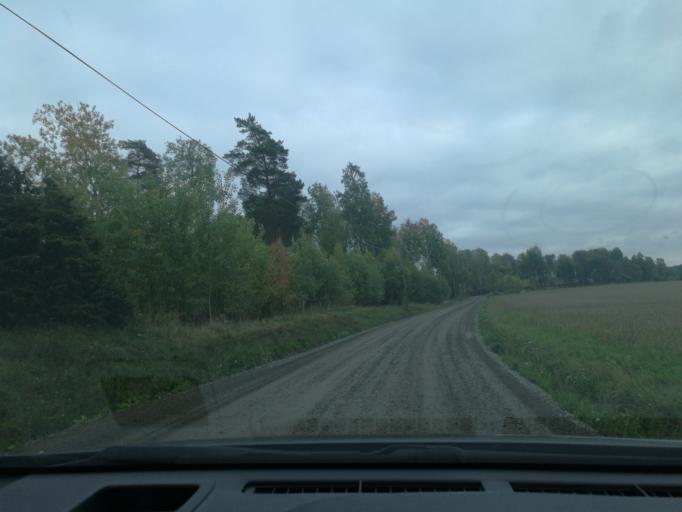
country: SE
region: Vaestmanland
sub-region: Vasteras
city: Tillberga
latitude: 59.7409
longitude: 16.6969
